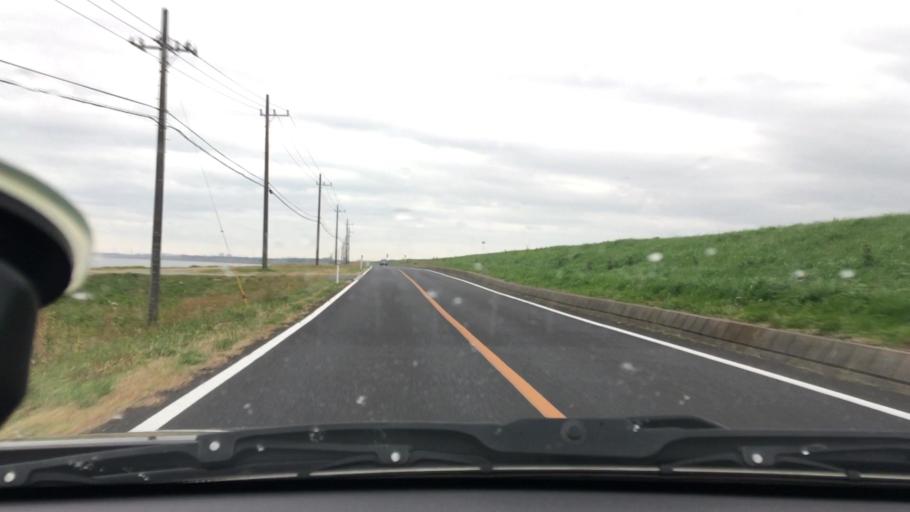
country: JP
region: Chiba
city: Omigawa
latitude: 35.8597
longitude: 140.6463
